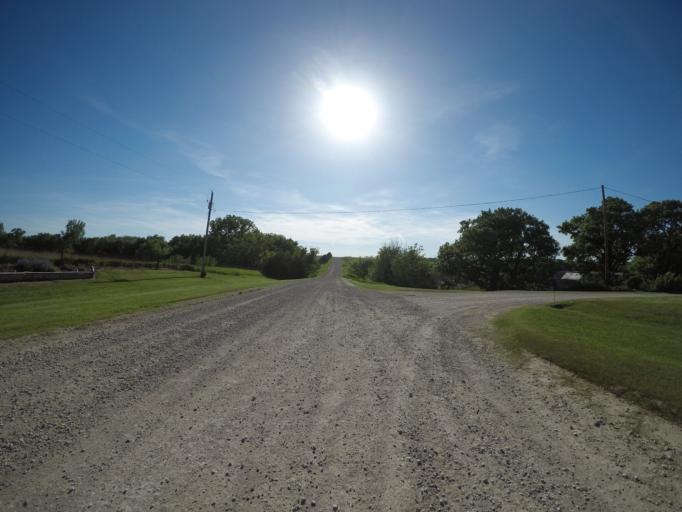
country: US
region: Kansas
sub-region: Clay County
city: Clay Center
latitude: 39.5103
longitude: -97.0092
